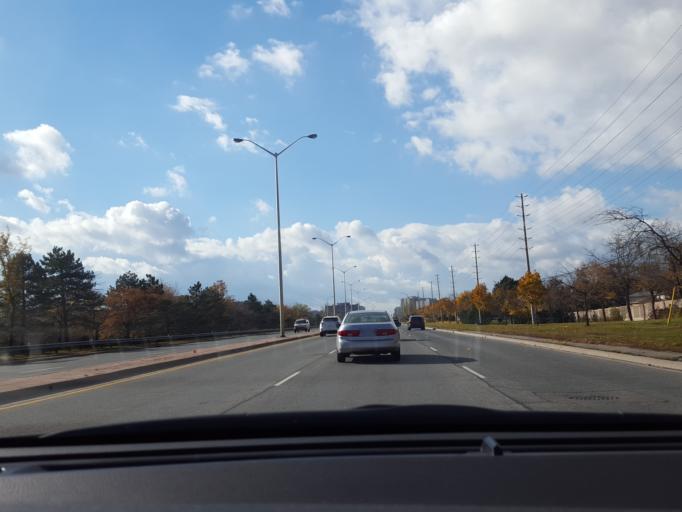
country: CA
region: Ontario
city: Brampton
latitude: 43.7314
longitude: -79.7099
